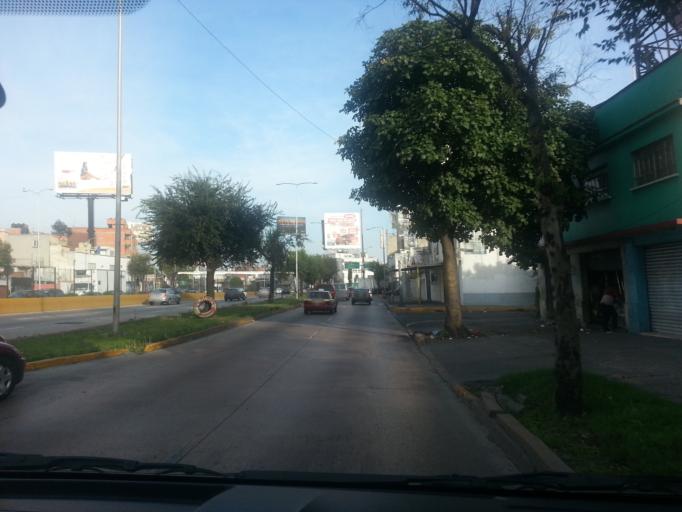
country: MX
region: Mexico City
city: Cuauhtemoc
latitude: 19.4644
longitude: -99.1320
